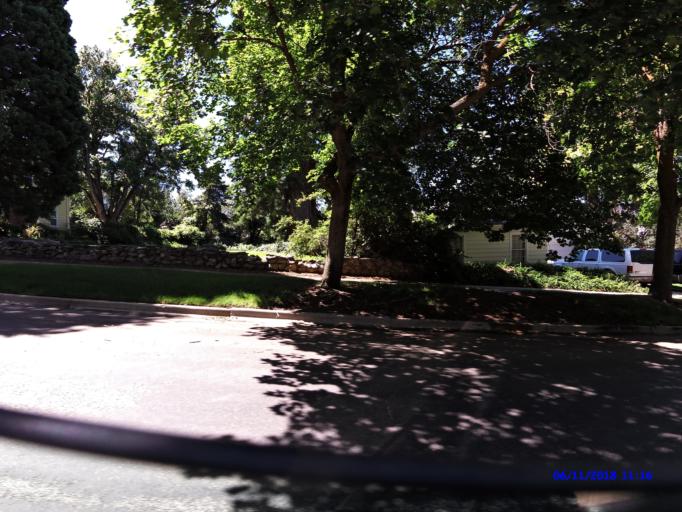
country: US
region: Utah
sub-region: Weber County
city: Ogden
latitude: 41.2213
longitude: -111.9396
